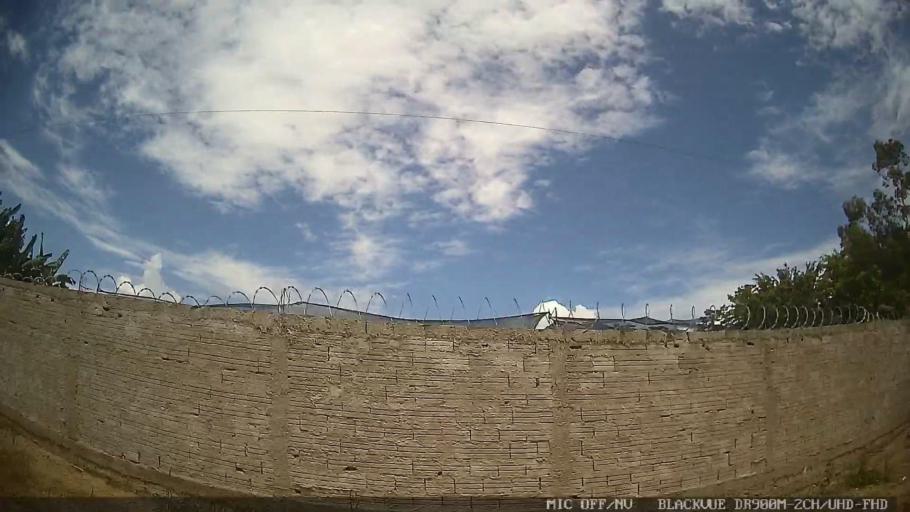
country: BR
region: Sao Paulo
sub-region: Conchas
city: Conchas
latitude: -23.0890
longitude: -47.9816
